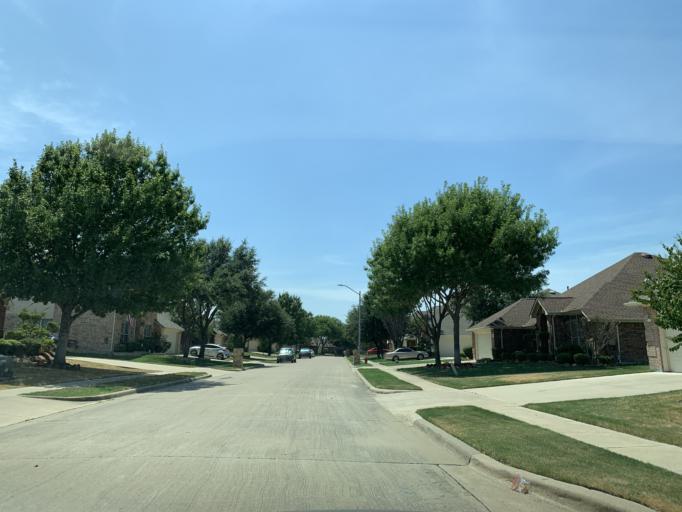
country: US
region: Texas
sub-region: Dallas County
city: Cedar Hill
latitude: 32.6456
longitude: -97.0153
